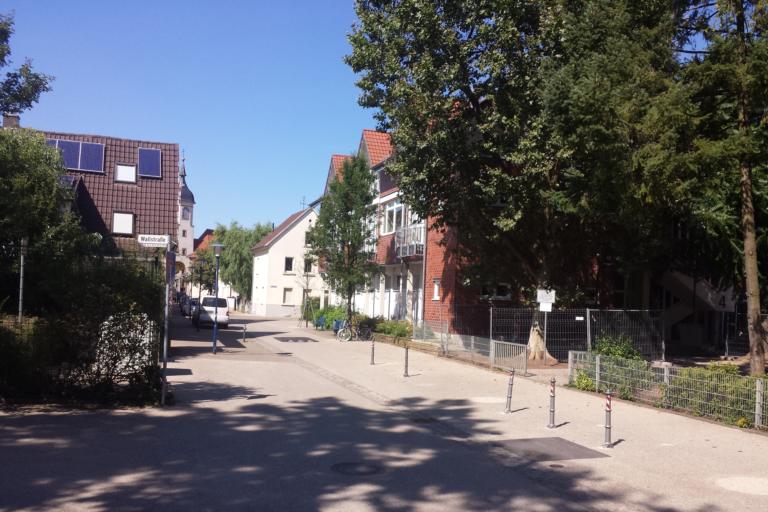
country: DE
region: Baden-Wuerttemberg
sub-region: Karlsruhe Region
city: Eppelheim
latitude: 49.4226
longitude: 8.6490
